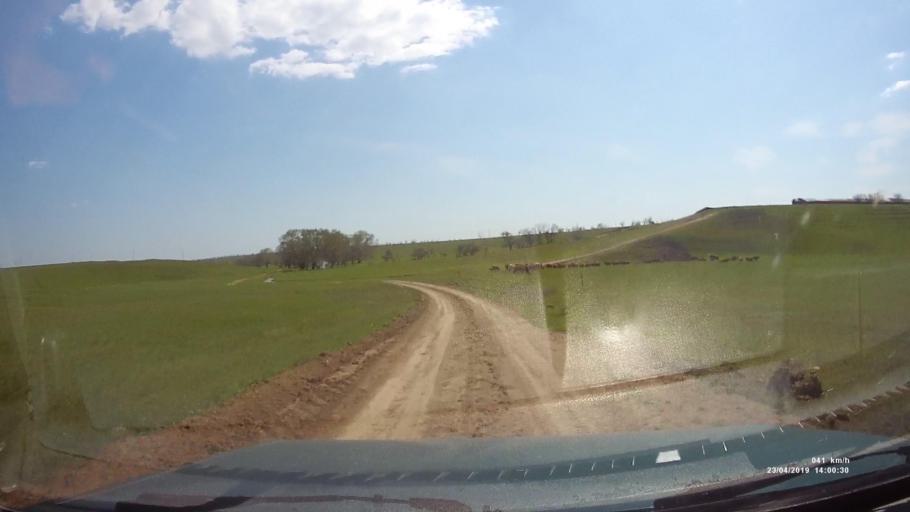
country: RU
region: Rostov
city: Remontnoye
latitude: 46.5591
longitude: 42.9469
